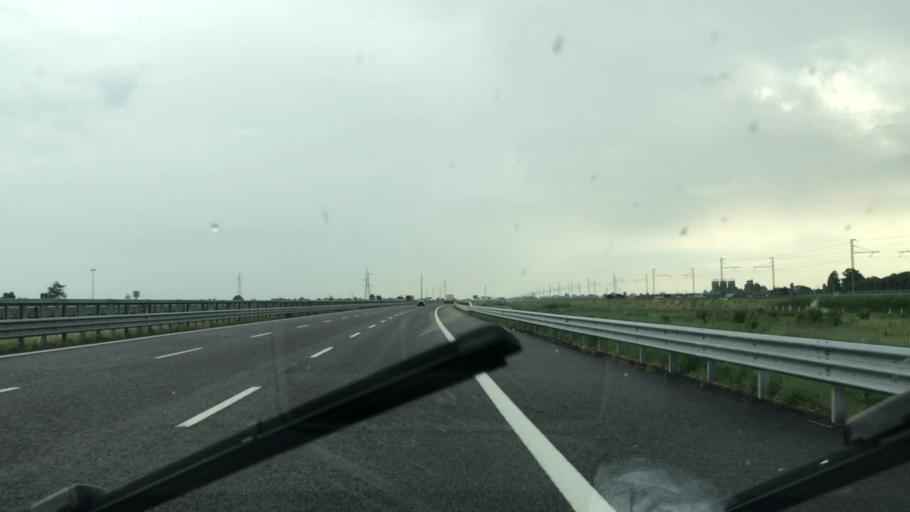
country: IT
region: Lombardy
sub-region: Provincia di Bergamo
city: Antegnate
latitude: 45.4957
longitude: 9.8090
